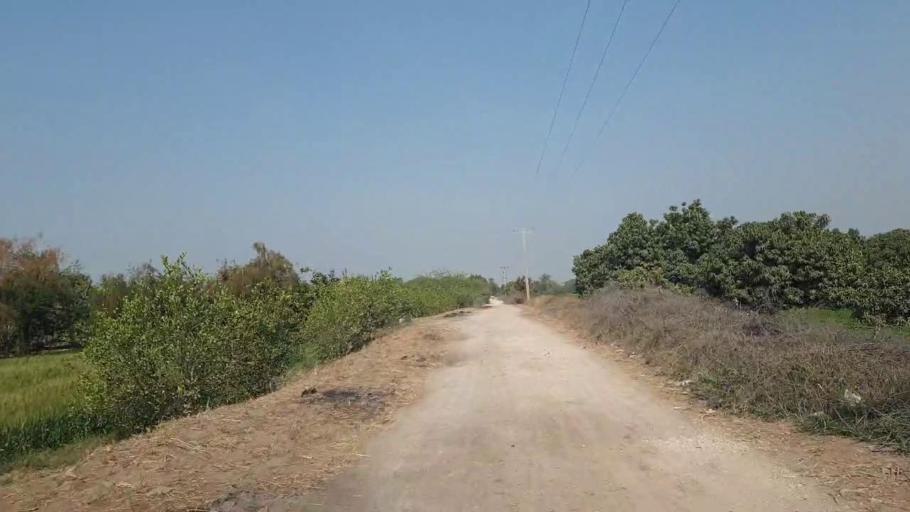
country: PK
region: Sindh
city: Chambar
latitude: 25.4069
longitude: 68.8958
